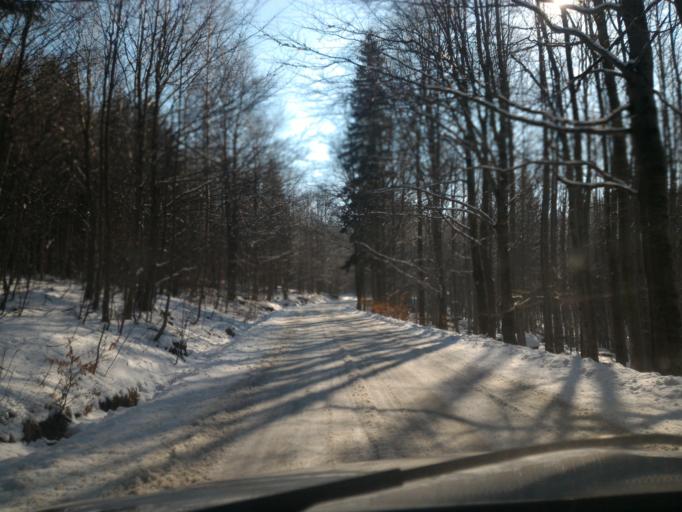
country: CZ
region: Liberecky
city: Nove Mesto pod Smrkem
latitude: 50.8672
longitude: 15.2480
